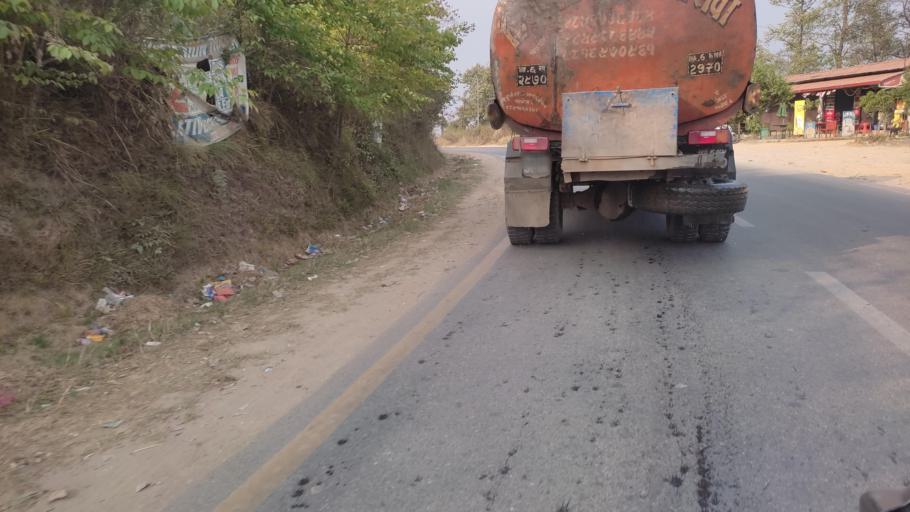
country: NP
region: Central Region
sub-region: Bagmati Zone
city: Patan
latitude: 27.6613
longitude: 85.2946
